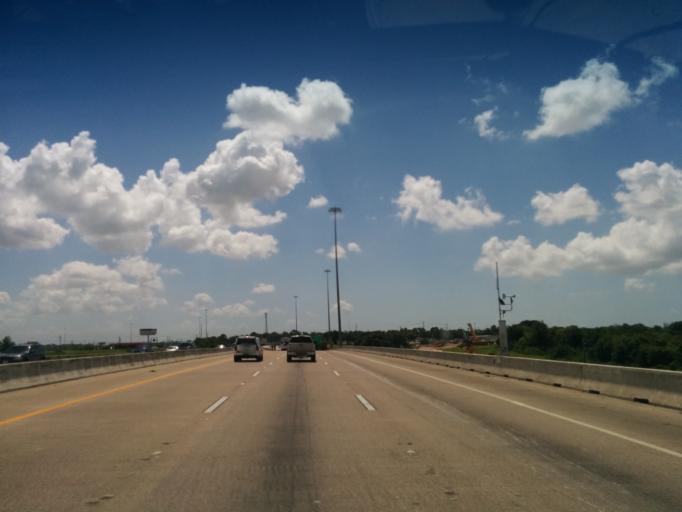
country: US
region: Texas
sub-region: Harris County
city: Highlands
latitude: 29.7928
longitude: -95.0620
